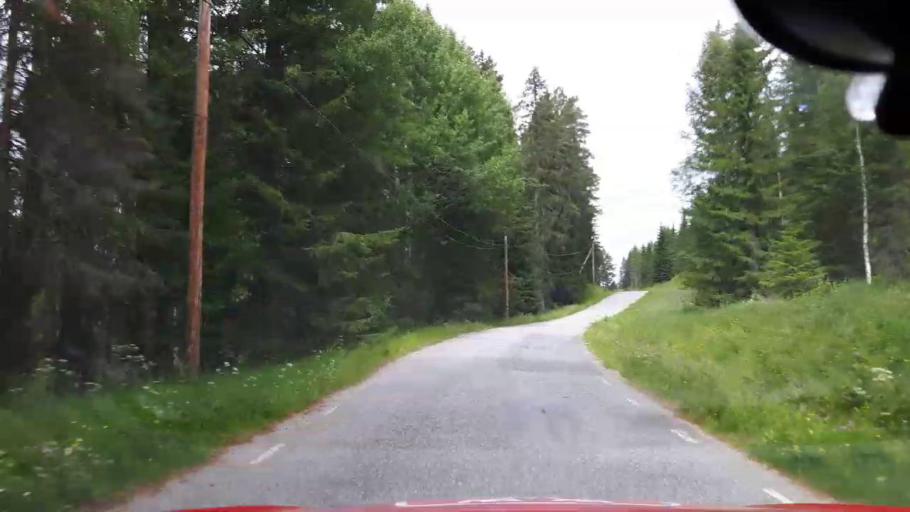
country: SE
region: Jaemtland
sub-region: Braecke Kommun
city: Braecke
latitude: 62.8630
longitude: 15.2738
